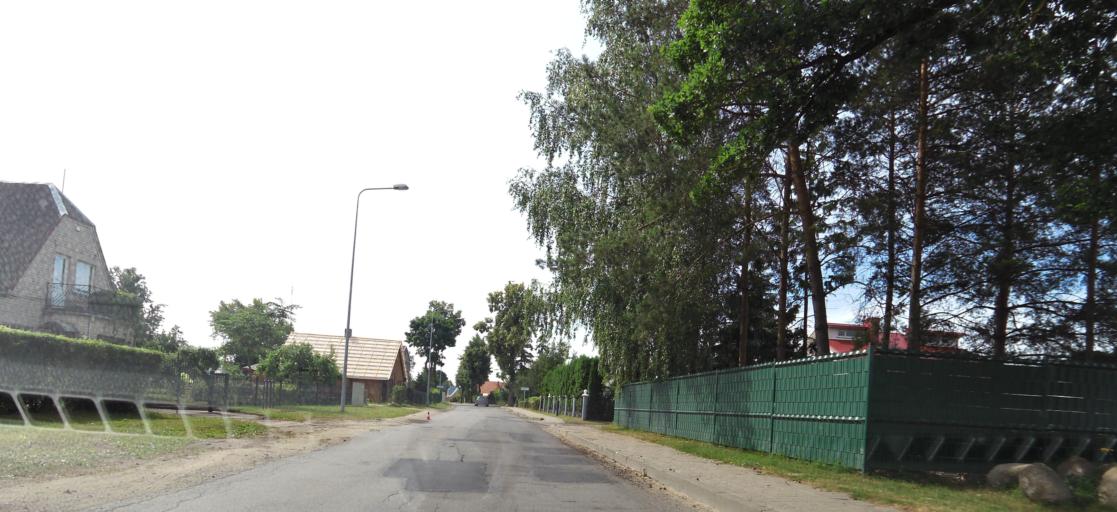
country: LT
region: Panevezys
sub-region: Birzai
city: Birzai
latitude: 56.2016
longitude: 24.7667
